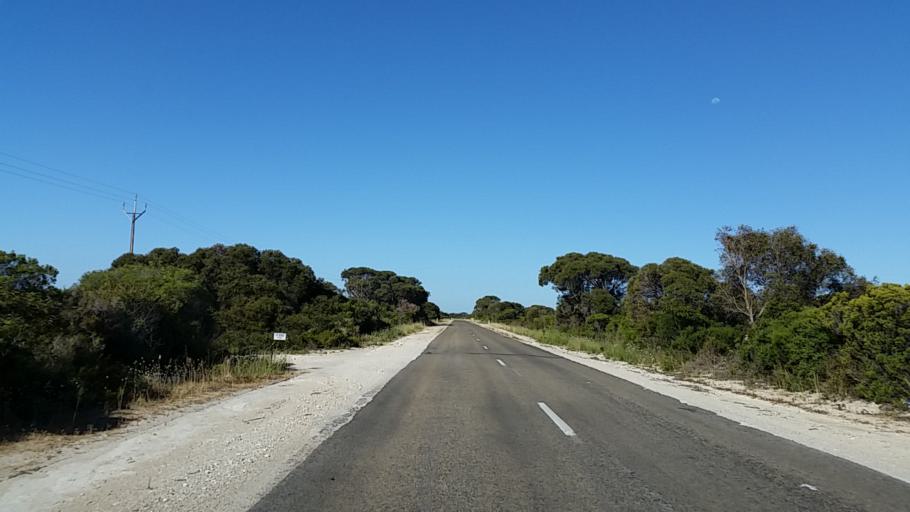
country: AU
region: South Australia
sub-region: Yorke Peninsula
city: Honiton
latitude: -35.2212
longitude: 136.9961
